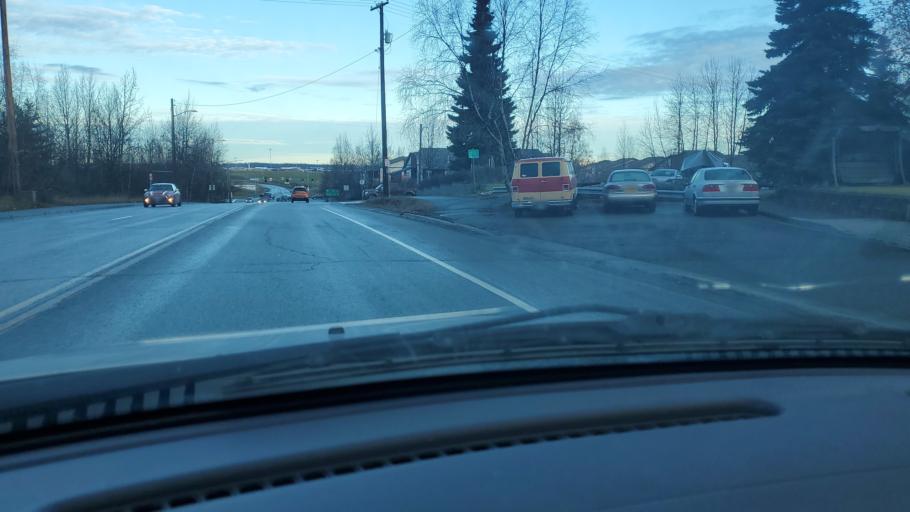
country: US
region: Alaska
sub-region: Anchorage Municipality
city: Anchorage
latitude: 61.2055
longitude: -149.8383
